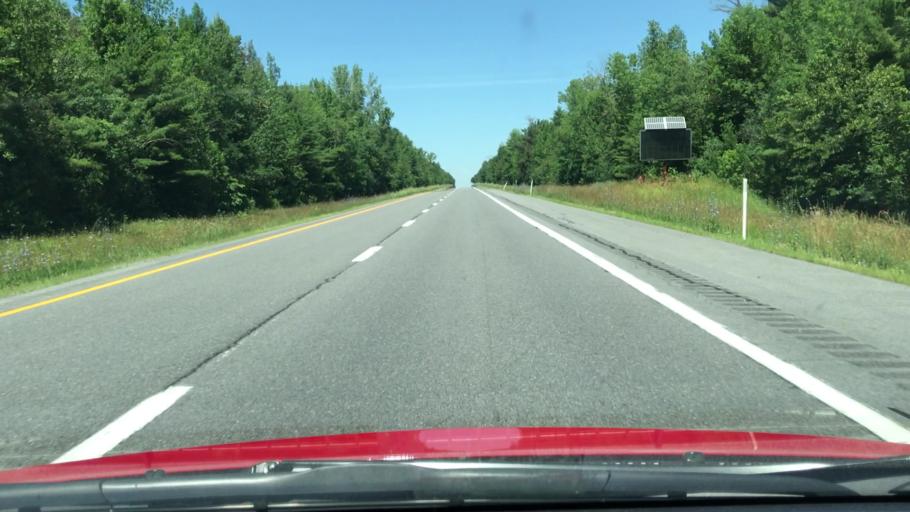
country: US
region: New York
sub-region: Clinton County
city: Champlain
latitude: 44.9540
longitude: -73.4485
